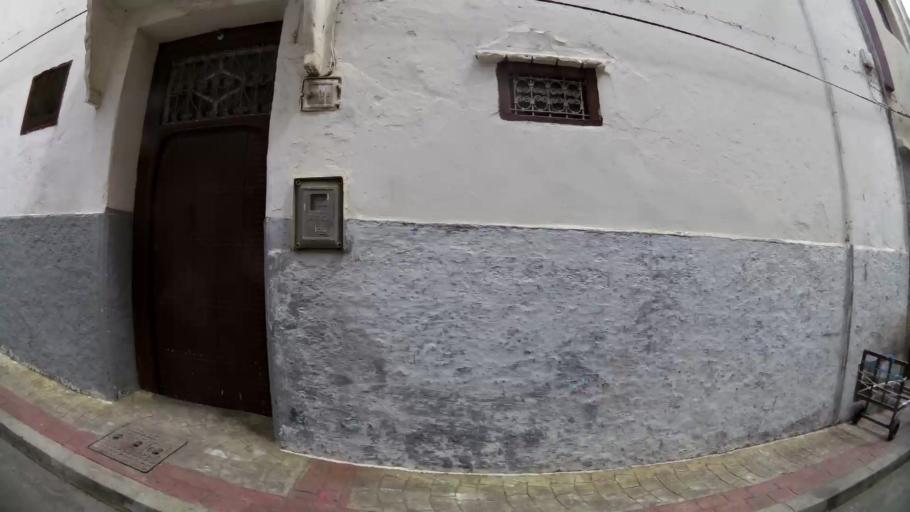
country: MA
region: Tanger-Tetouan
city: Tetouan
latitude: 35.5753
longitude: -5.3582
